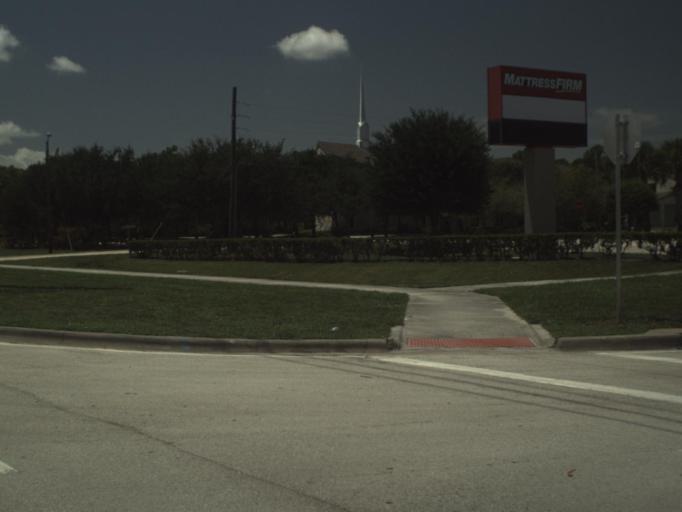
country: US
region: Florida
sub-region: Martin County
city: North River Shores
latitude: 27.2295
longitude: -80.2664
